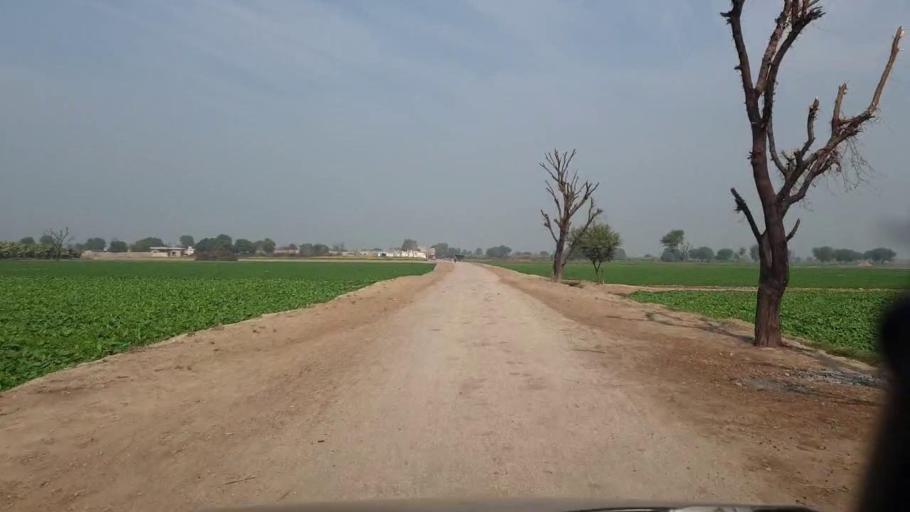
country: PK
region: Sindh
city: Shahdadpur
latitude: 26.0102
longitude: 68.5101
